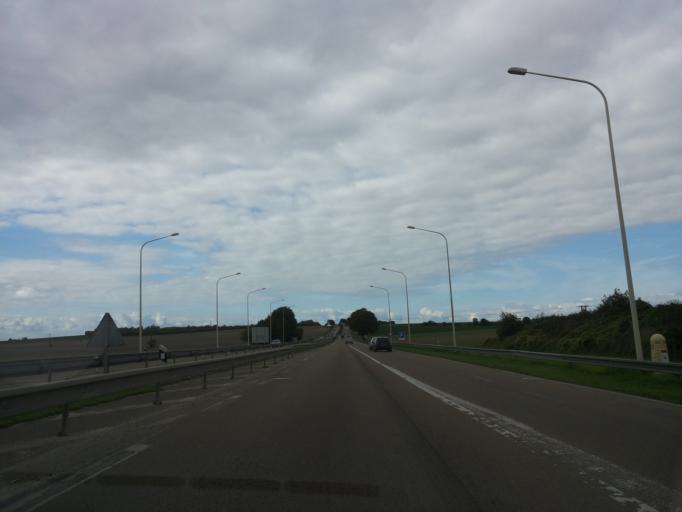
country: FR
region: Champagne-Ardenne
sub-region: Departement de la Marne
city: Sillery
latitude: 49.2099
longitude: 4.1446
